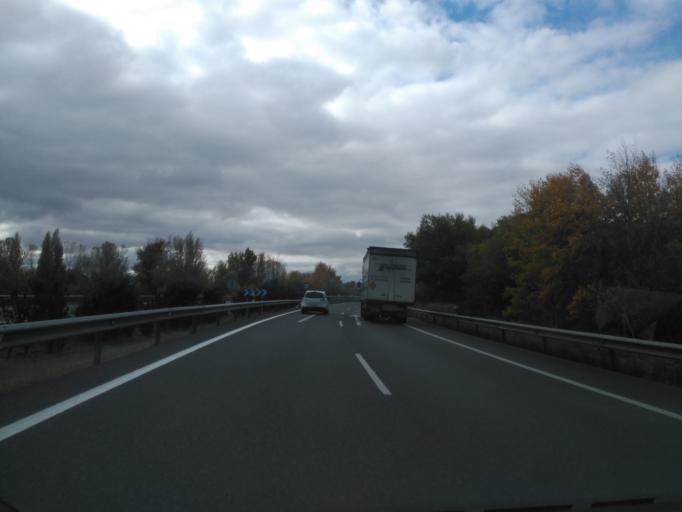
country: ES
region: Castille and Leon
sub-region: Provincia de Palencia
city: Duenas
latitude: 41.8914
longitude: -4.5257
